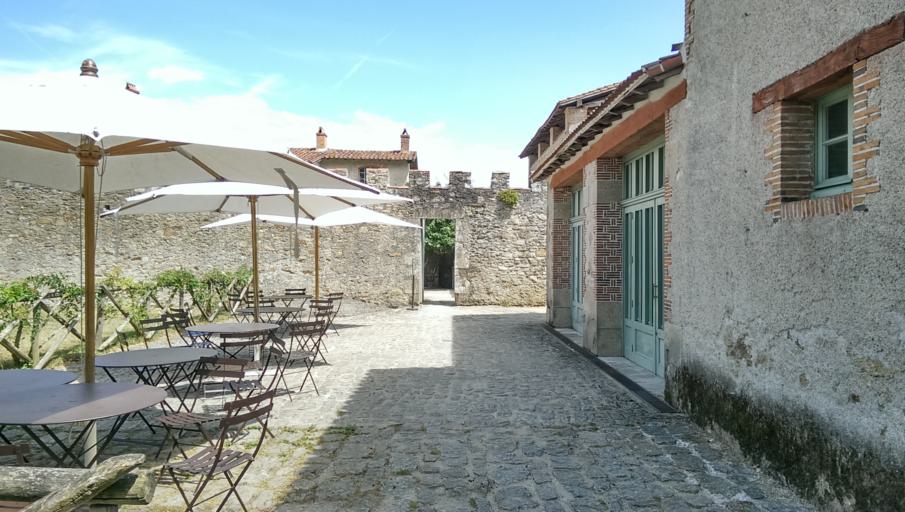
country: FR
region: Pays de la Loire
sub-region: Departement de la Loire-Atlantique
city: Clisson
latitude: 47.0859
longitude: -1.2747
